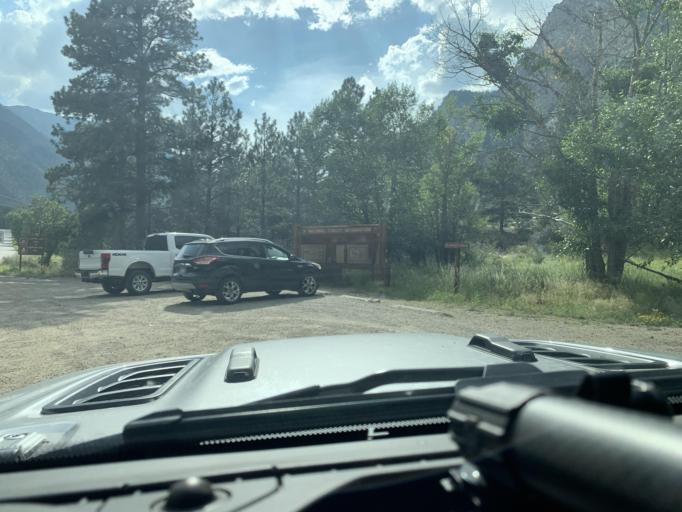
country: US
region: Colorado
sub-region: Chaffee County
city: Buena Vista
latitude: 38.7175
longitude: -106.1992
